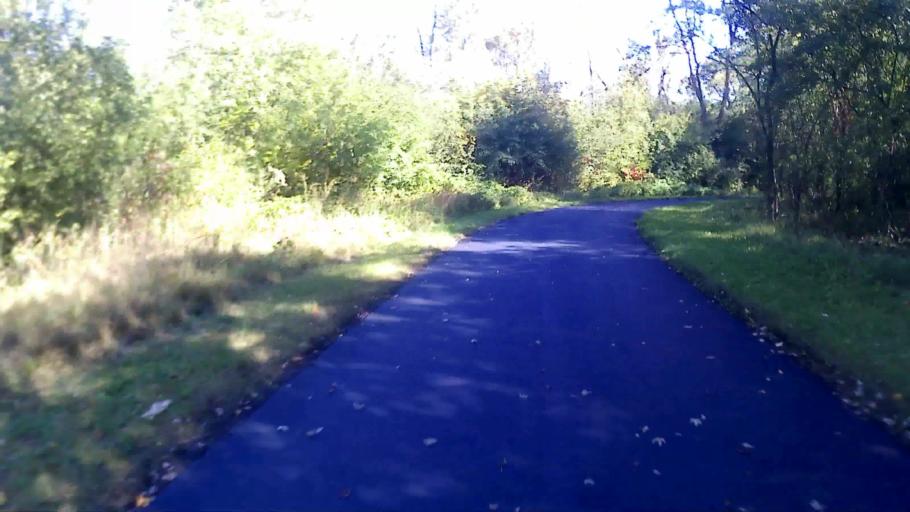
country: US
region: Illinois
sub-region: DuPage County
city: Villa Park
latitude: 41.9082
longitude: -87.9679
